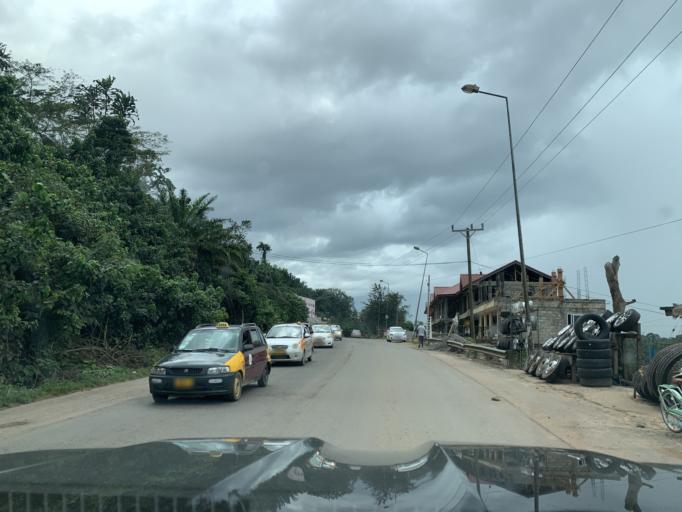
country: GH
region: Western
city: Tarkwa
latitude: 5.3252
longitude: -1.9828
